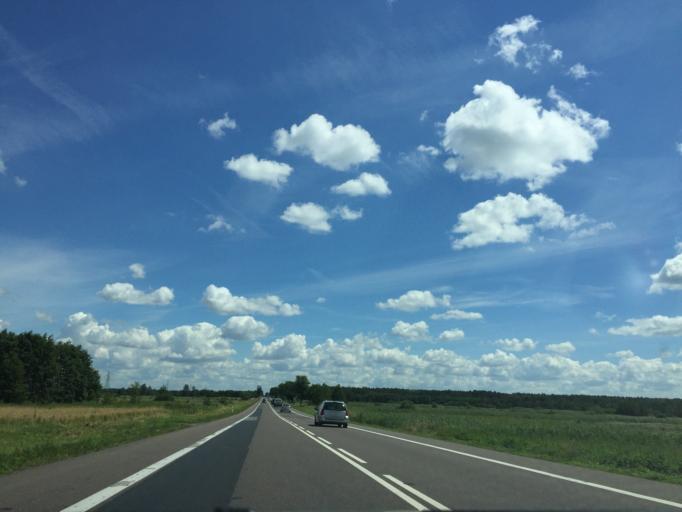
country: PL
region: Lublin Voivodeship
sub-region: Powiat swidnicki
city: Trawniki
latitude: 51.1605
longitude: 22.9534
